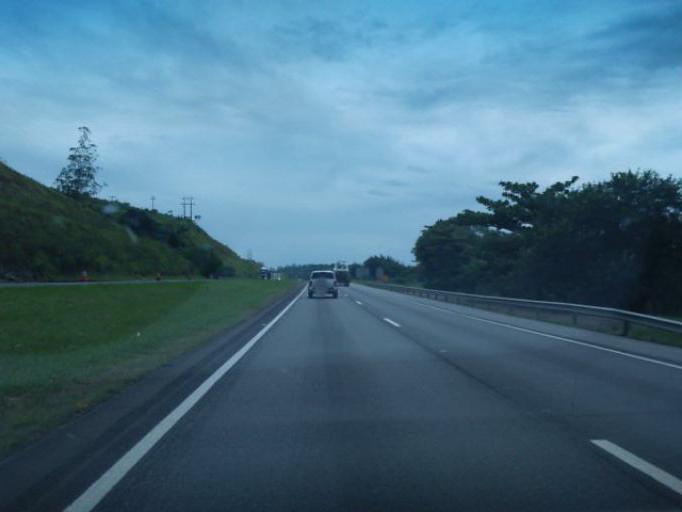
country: BR
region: Sao Paulo
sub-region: Juquia
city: Juquia
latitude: -24.3270
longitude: -47.5674
